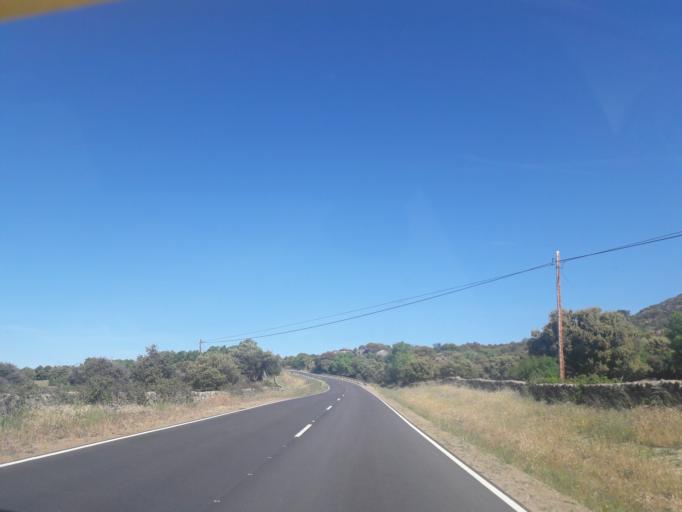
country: ES
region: Castille and Leon
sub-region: Provincia de Salamanca
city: Nava de Bejar
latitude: 40.4825
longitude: -5.6455
